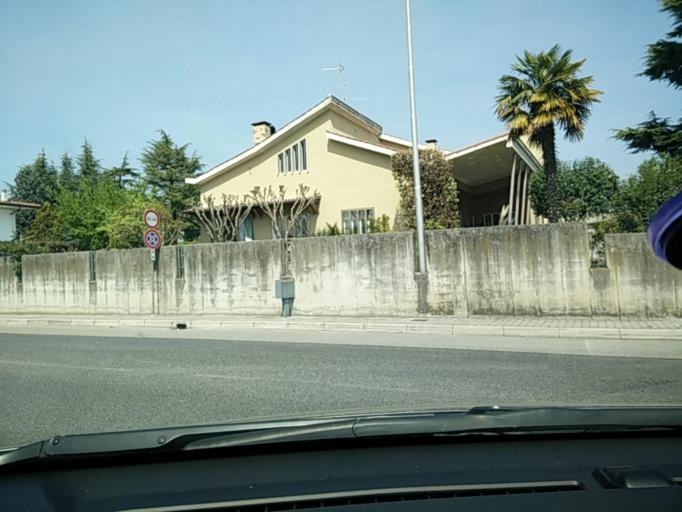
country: IT
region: Friuli Venezia Giulia
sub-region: Provincia di Udine
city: Manzano
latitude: 45.9874
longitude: 13.3705
